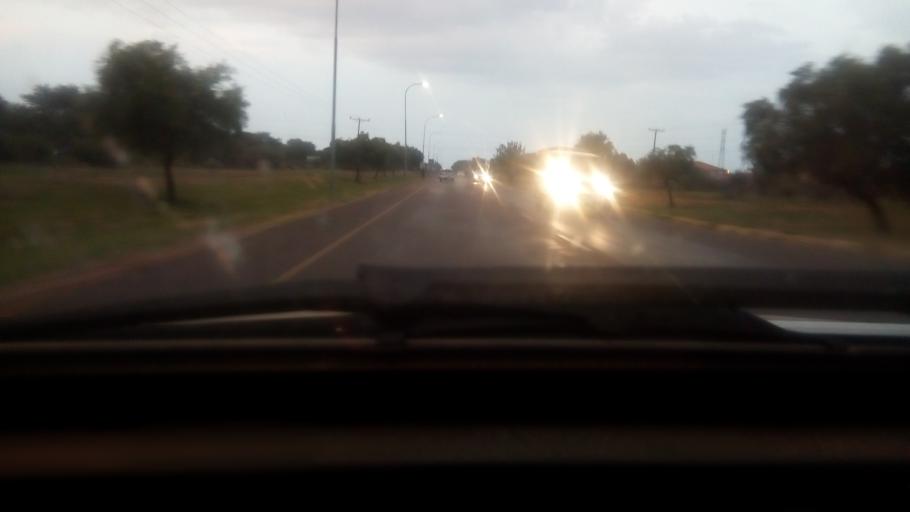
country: BW
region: Kweneng
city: Mmopone
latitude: -24.5966
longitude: 25.9201
